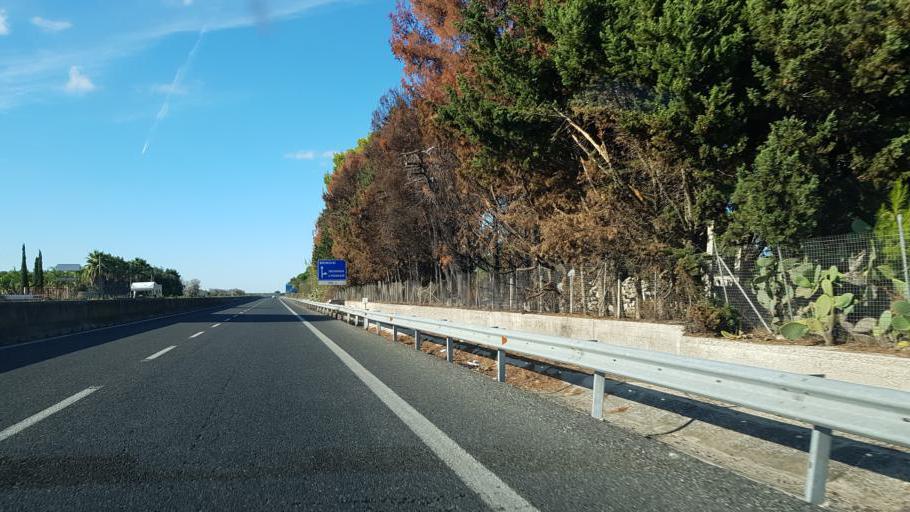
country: IT
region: Apulia
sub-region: Provincia di Brindisi
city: Torchiarolo
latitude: 40.4770
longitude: 18.0471
